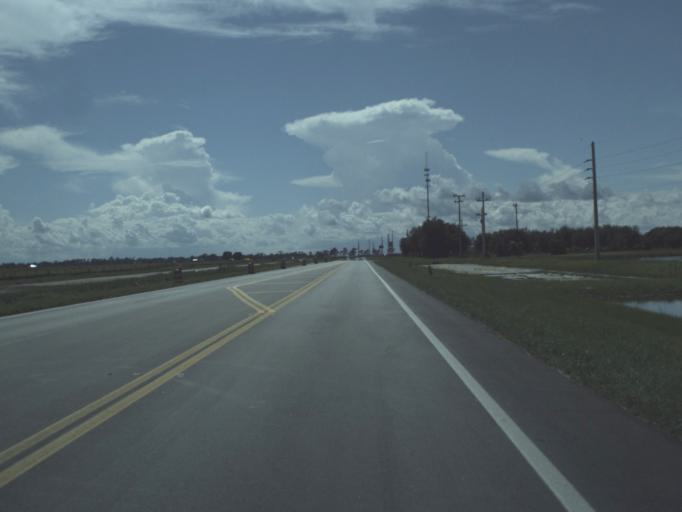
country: US
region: Florida
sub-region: Okeechobee County
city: Taylor Creek
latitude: 27.2907
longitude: -80.6983
